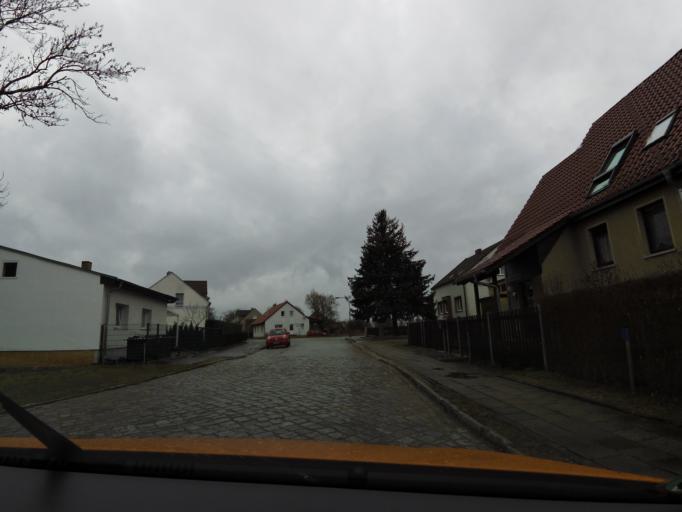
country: DE
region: Brandenburg
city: Sperenberg
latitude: 52.1671
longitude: 13.3634
